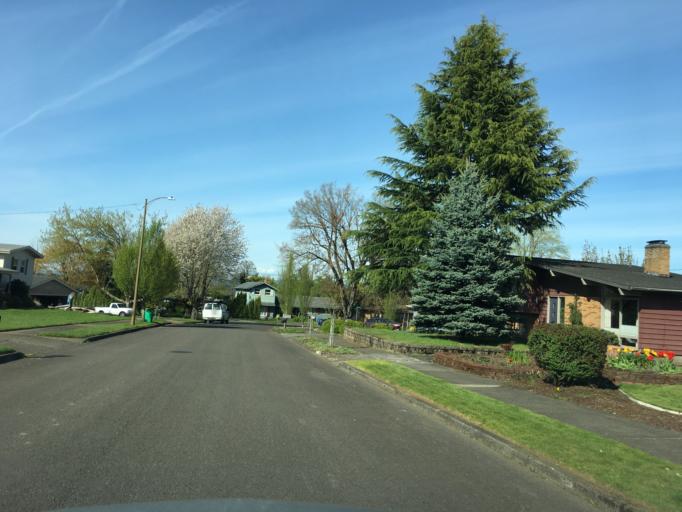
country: US
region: Oregon
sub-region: Multnomah County
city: Lents
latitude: 45.5425
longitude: -122.5208
